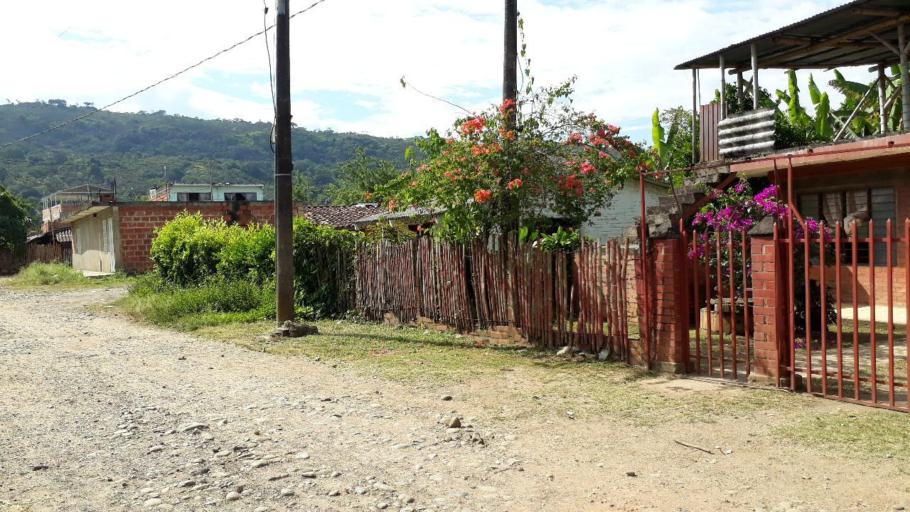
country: CO
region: Valle del Cauca
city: Jamundi
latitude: 3.1708
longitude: -76.5932
